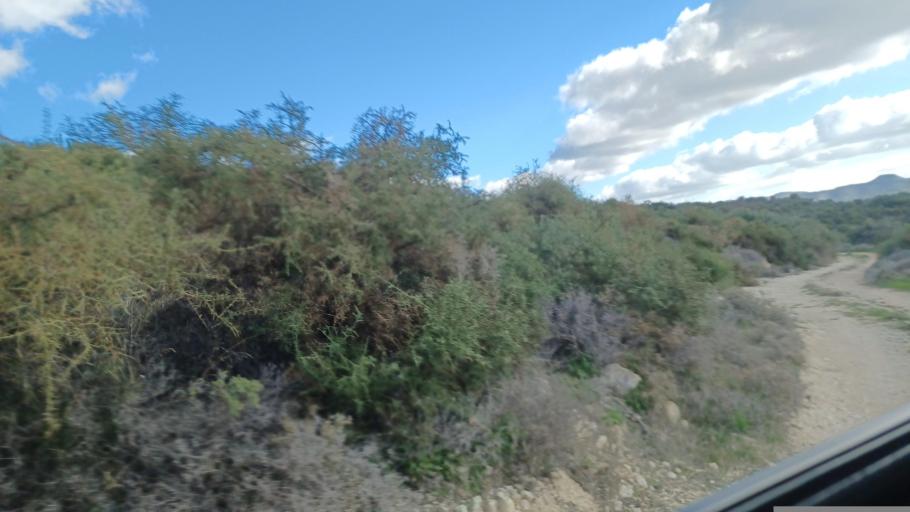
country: CY
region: Limassol
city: Pano Polemidia
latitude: 34.7692
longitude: 32.9800
